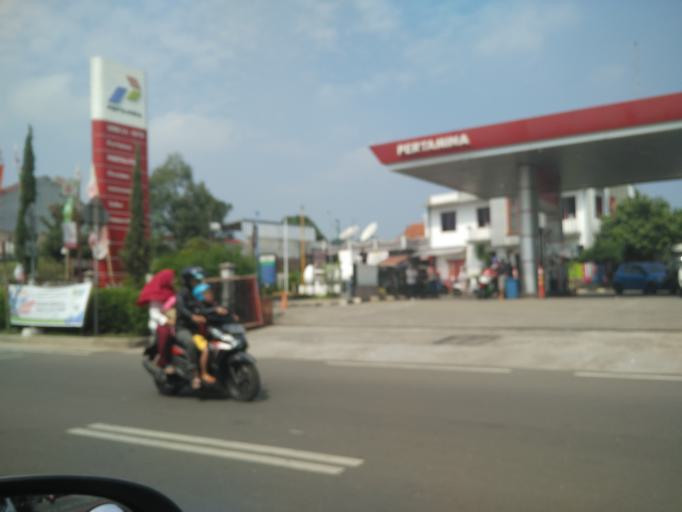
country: ID
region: West Java
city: Caringin
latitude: -6.6624
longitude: 106.8541
